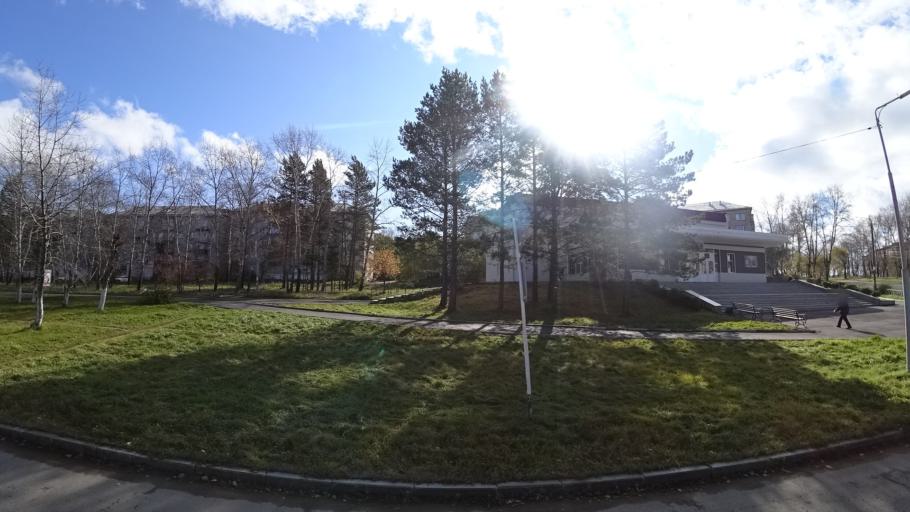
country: RU
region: Khabarovsk Krai
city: Amursk
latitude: 50.2224
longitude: 136.9036
